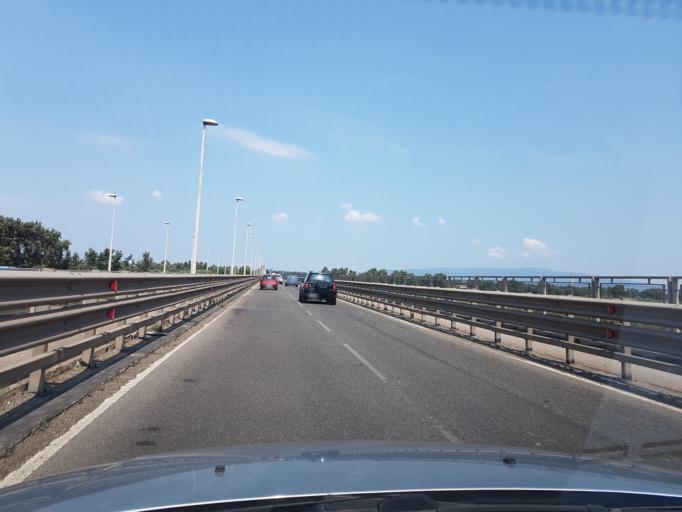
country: IT
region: Sardinia
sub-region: Provincia di Oristano
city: Donigala Fenugheddu
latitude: 39.9178
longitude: 8.5838
